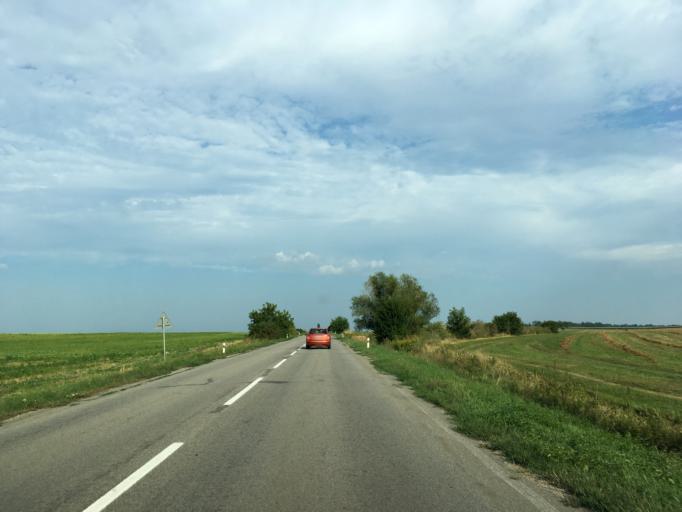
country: SK
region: Nitriansky
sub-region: Okres Komarno
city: Hurbanovo
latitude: 47.9061
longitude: 18.3332
